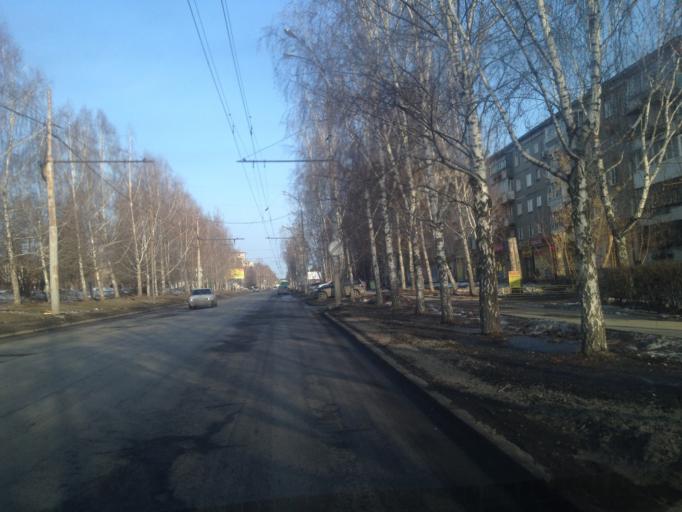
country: RU
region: Sverdlovsk
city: Sovkhoznyy
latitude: 56.8008
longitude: 60.5713
